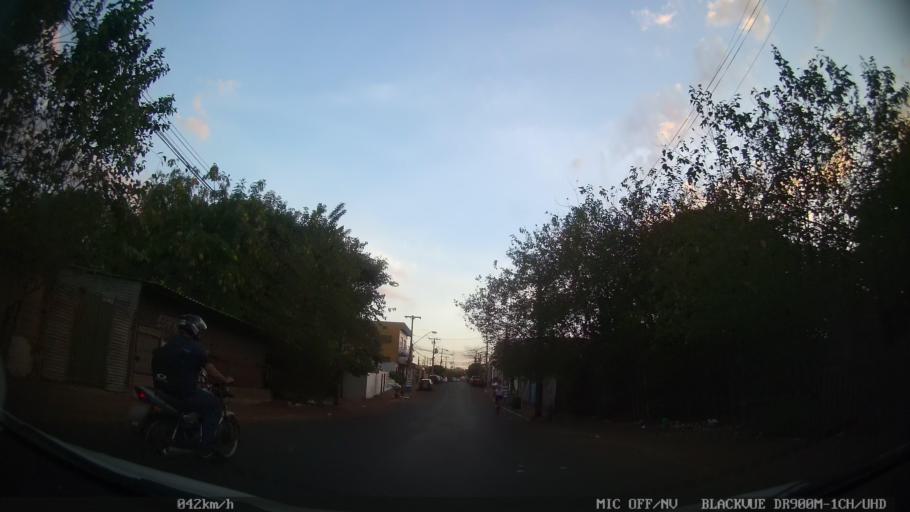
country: BR
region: Sao Paulo
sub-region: Ribeirao Preto
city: Ribeirao Preto
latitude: -21.1473
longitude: -47.8235
